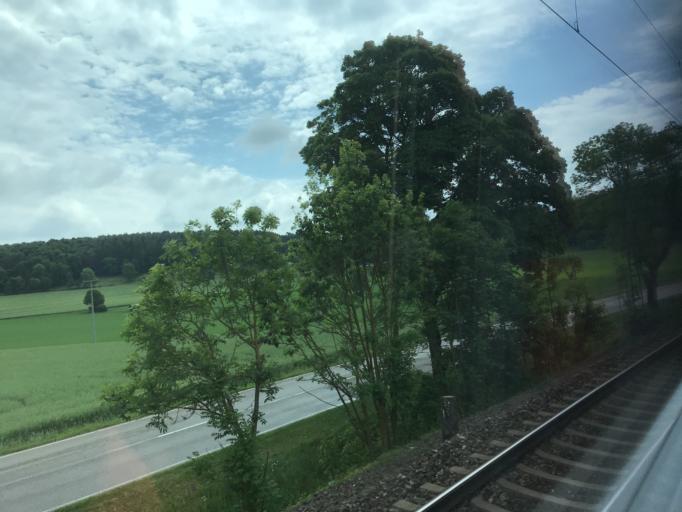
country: DE
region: Baden-Wuerttemberg
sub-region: Tuebingen Region
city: Amstetten
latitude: 48.5623
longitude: 9.8916
